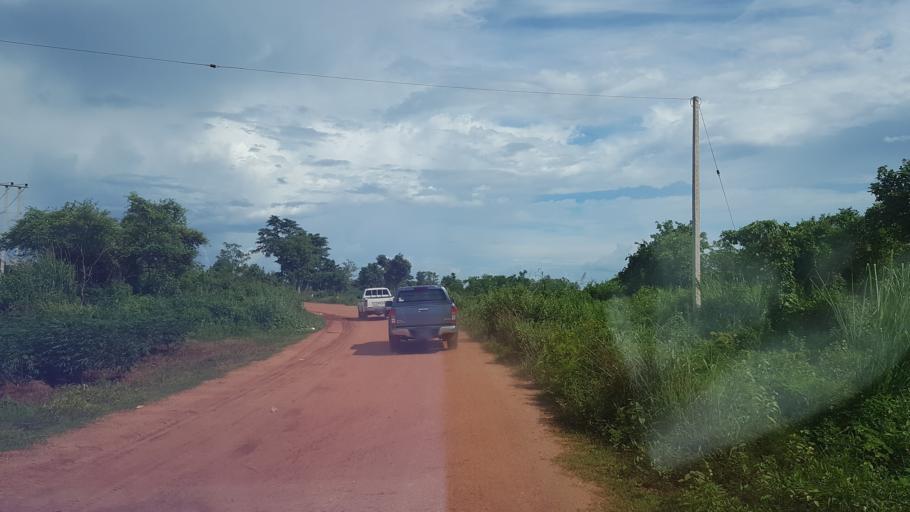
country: LA
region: Vientiane
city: Vientiane
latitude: 18.2059
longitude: 102.5679
